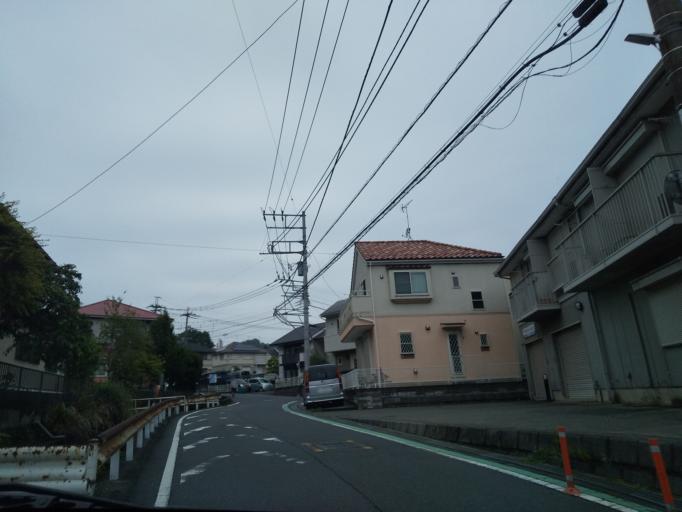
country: JP
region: Tokyo
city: Hino
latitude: 35.6491
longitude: 139.4267
